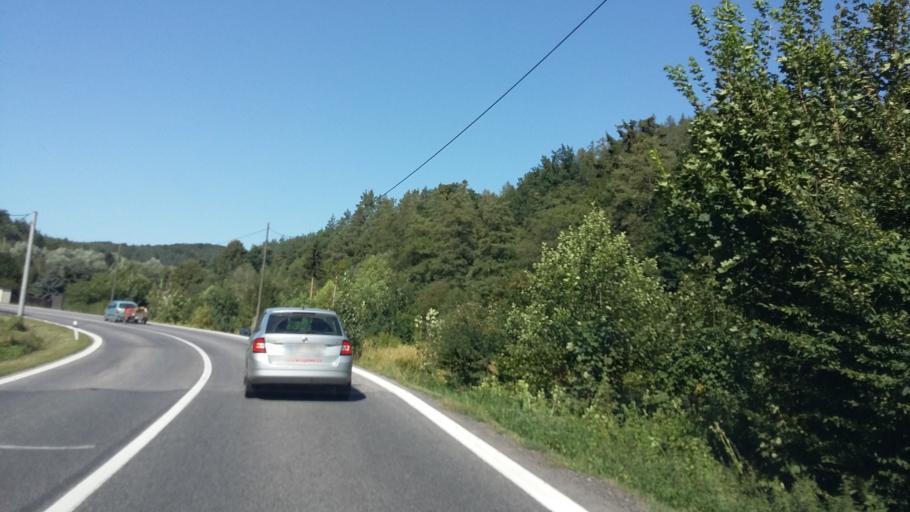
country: CZ
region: Central Bohemia
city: Dolni Berkovice
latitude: 50.4675
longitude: 14.4738
